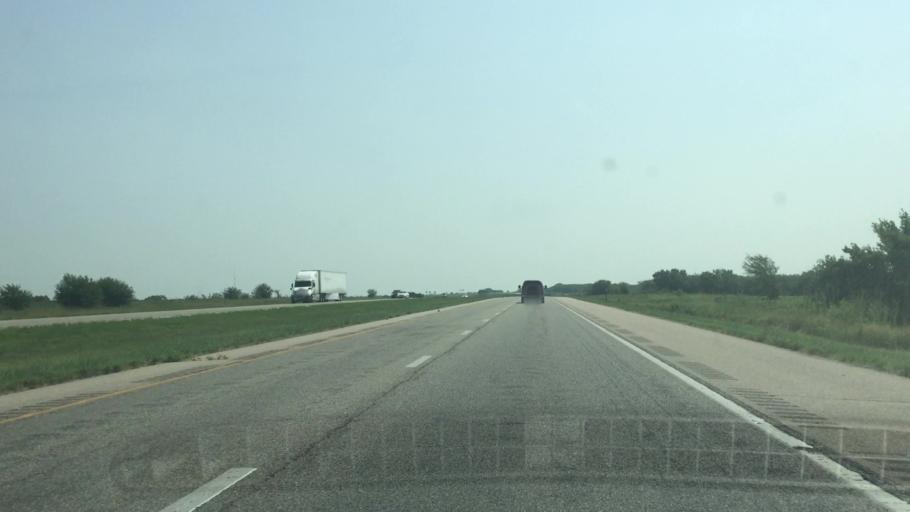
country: US
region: Kansas
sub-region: Osage County
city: Lyndon
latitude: 38.4264
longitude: -95.7637
